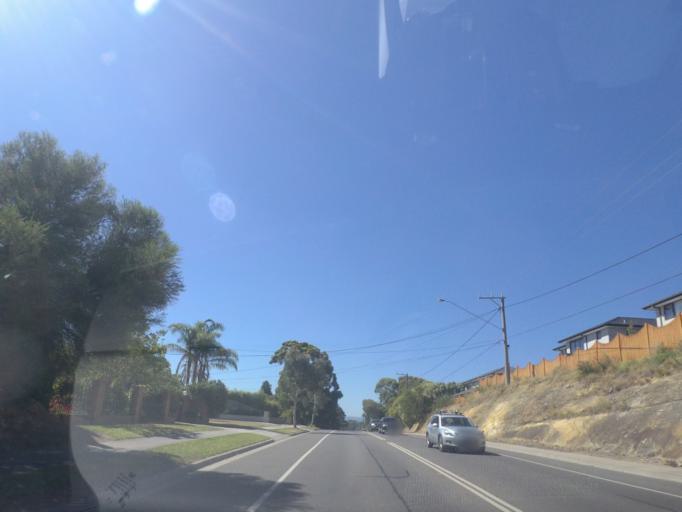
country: AU
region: Victoria
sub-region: Maroondah
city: Warranwood
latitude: -37.7892
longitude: 145.2477
